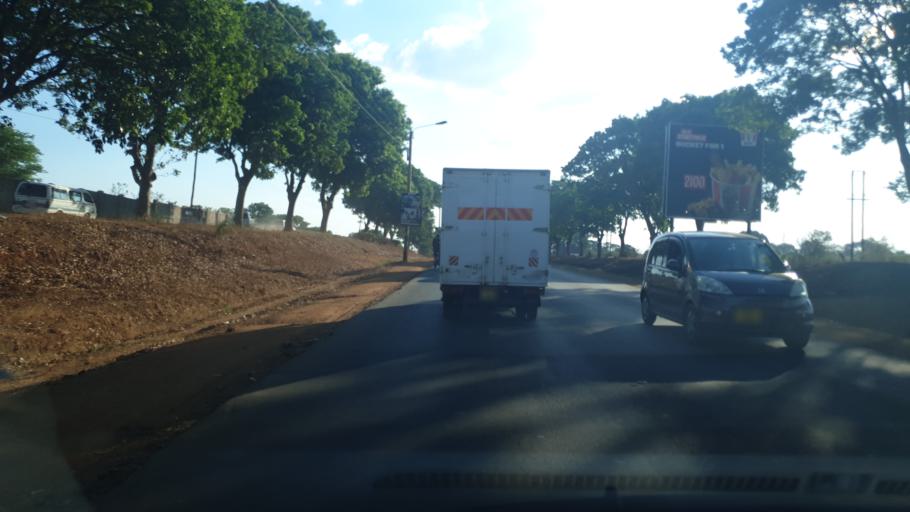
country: MW
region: Central Region
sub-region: Lilongwe District
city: Lilongwe
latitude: -13.9734
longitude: 33.7815
